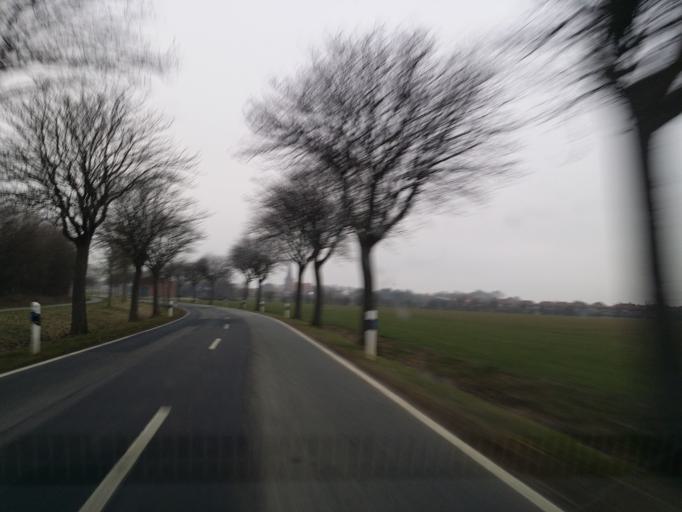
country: DE
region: Schleswig-Holstein
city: Grossenbrode
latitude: 54.4761
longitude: 11.0802
